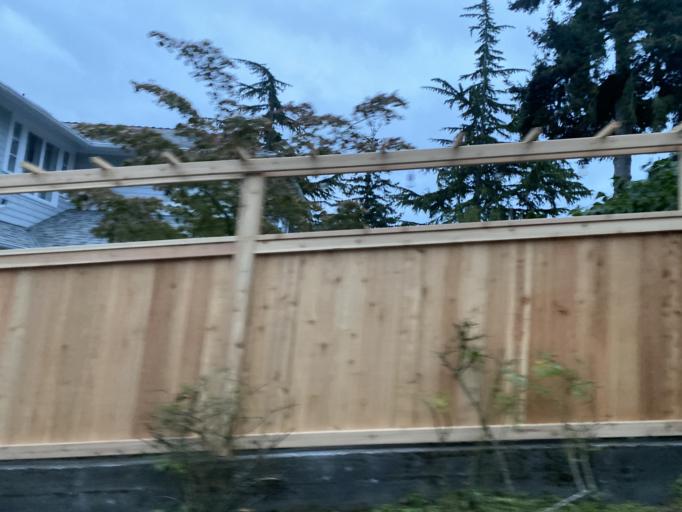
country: US
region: Washington
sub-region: King County
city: Seattle
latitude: 47.6495
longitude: -122.4050
